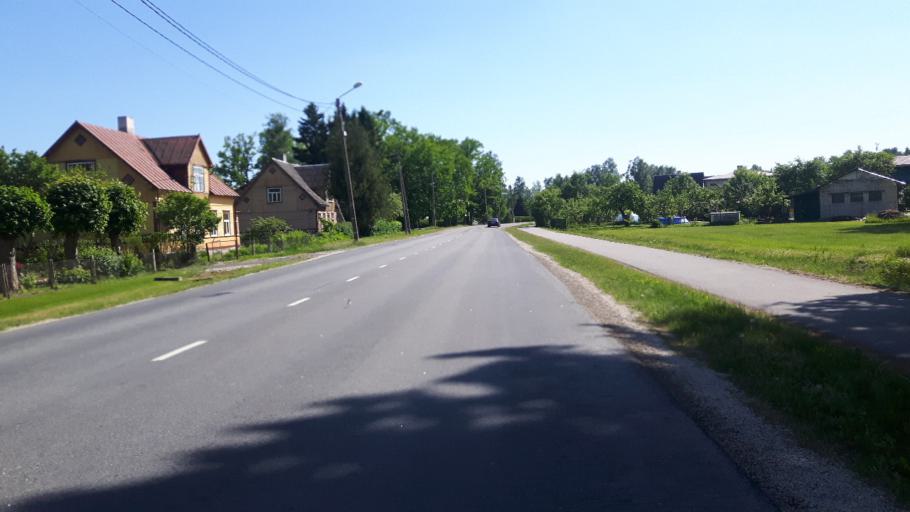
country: EE
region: Paernumaa
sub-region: Sindi linn
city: Sindi
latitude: 58.4014
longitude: 24.6463
